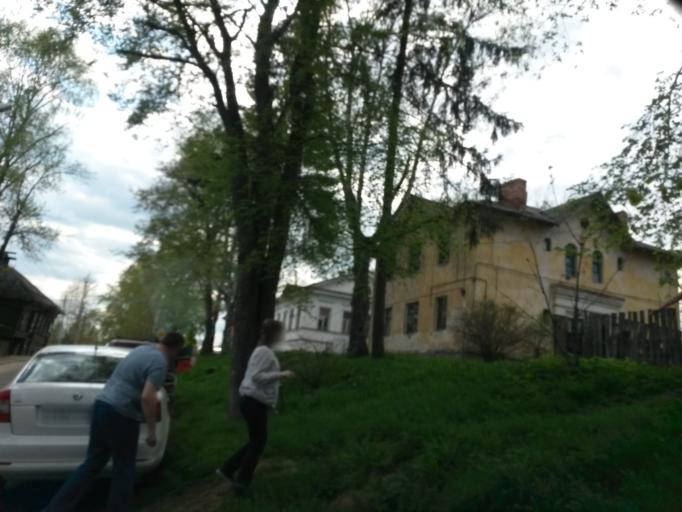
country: RU
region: Jaroslavl
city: Myshkin
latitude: 57.7814
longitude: 38.4778
